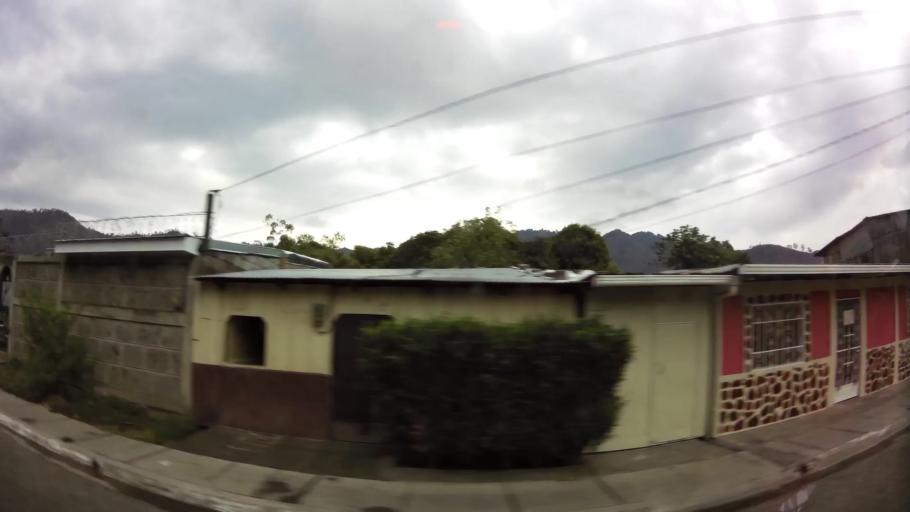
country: NI
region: Jinotega
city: Jinotega
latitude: 13.0852
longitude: -85.9979
